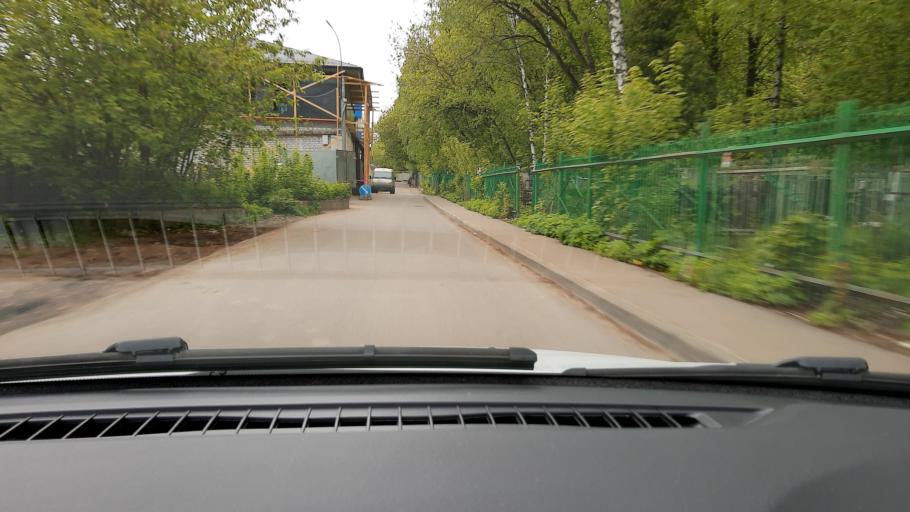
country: RU
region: Nizjnij Novgorod
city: Nizhniy Novgorod
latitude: 56.2808
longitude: 44.0003
